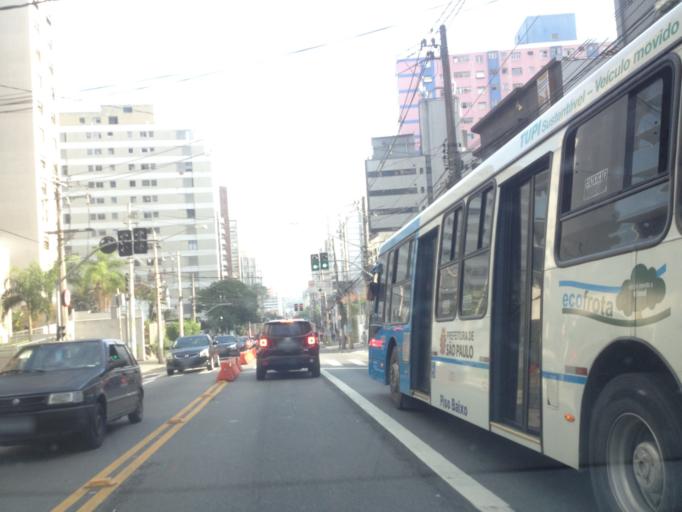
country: BR
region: Sao Paulo
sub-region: Sao Paulo
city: Sao Paulo
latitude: -23.5689
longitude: -46.6503
